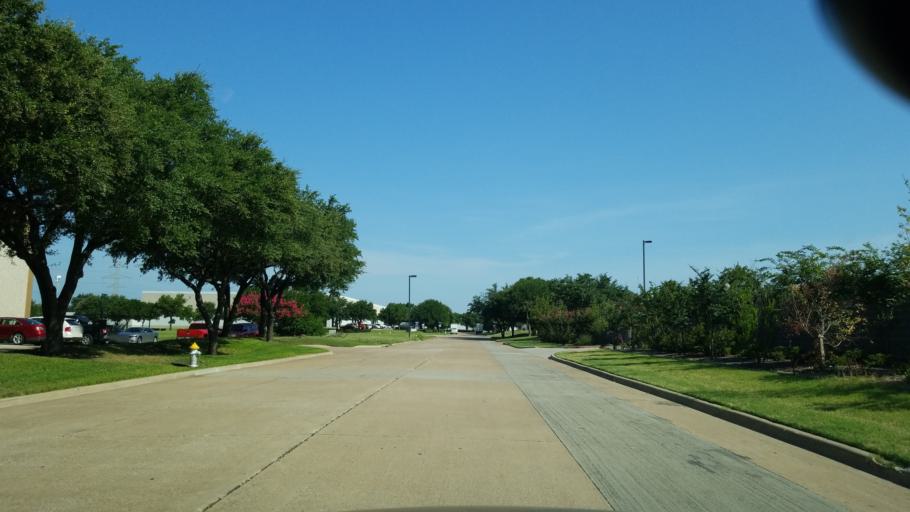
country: US
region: Texas
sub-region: Dallas County
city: Carrollton
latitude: 32.9582
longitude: -96.9166
